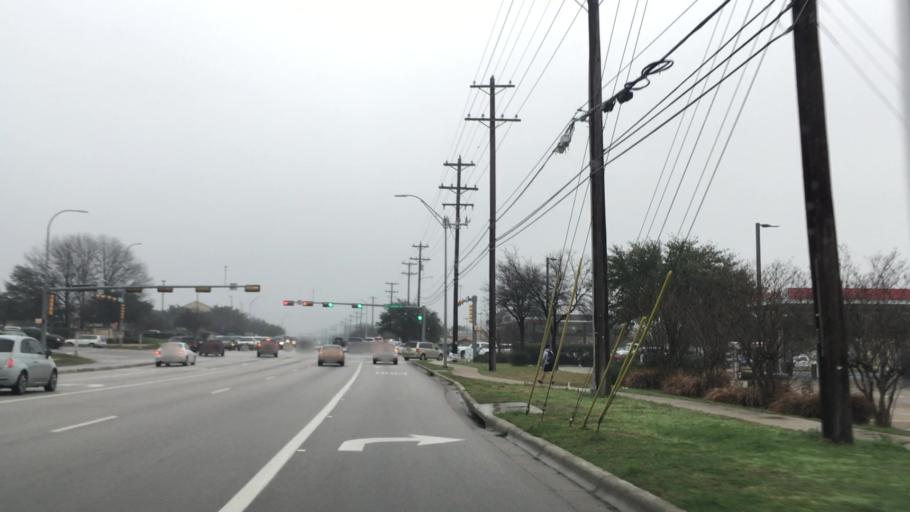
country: US
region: Texas
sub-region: Williamson County
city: Cedar Park
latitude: 30.4807
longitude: -97.8328
